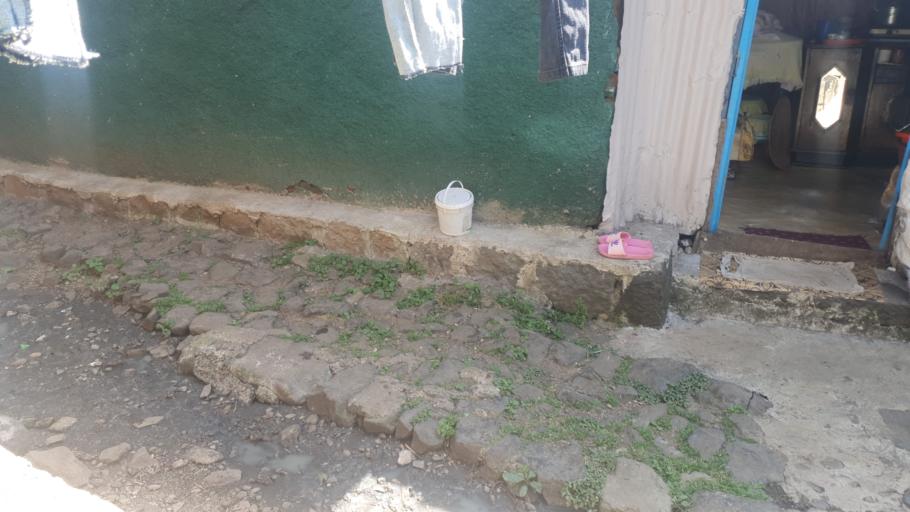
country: ET
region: Adis Abeba
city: Addis Ababa
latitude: 9.0197
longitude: 38.7410
